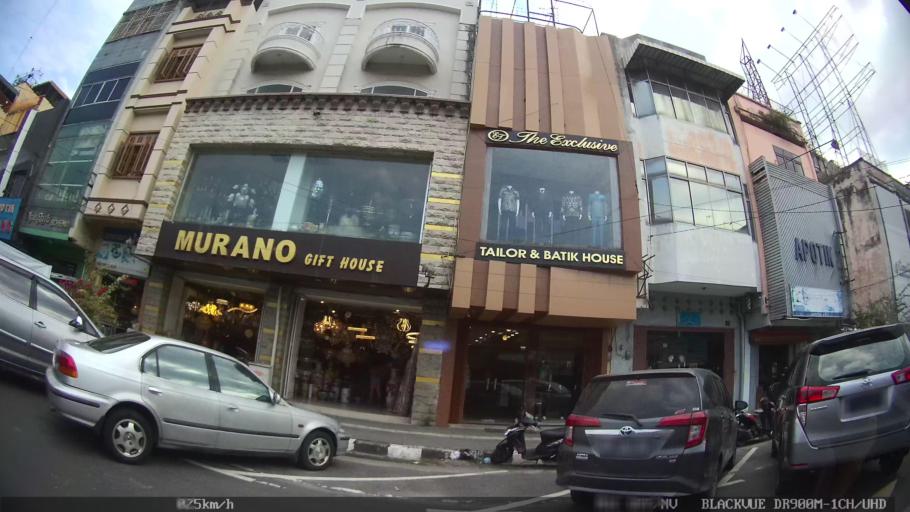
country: ID
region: North Sumatra
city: Medan
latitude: 3.5839
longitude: 98.6704
